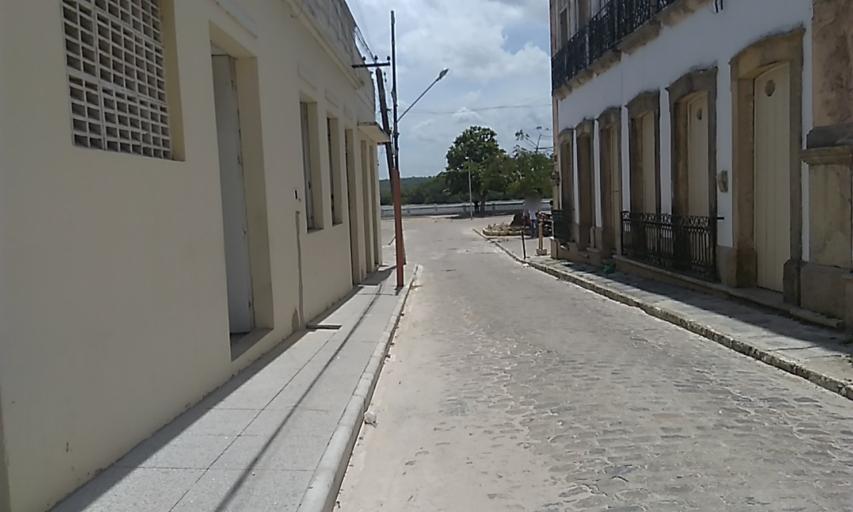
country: BR
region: Alagoas
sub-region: Penedo
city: Penedo
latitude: -10.2909
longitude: -36.5861
